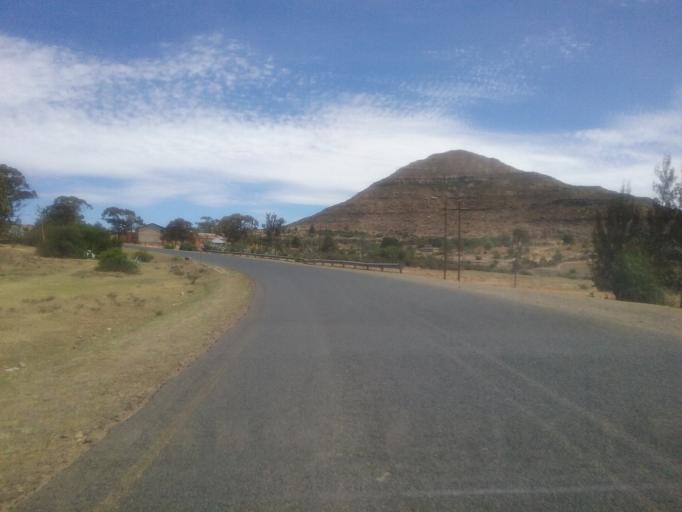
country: LS
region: Mafeteng
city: Mafeteng
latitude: -29.9547
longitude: 27.2869
